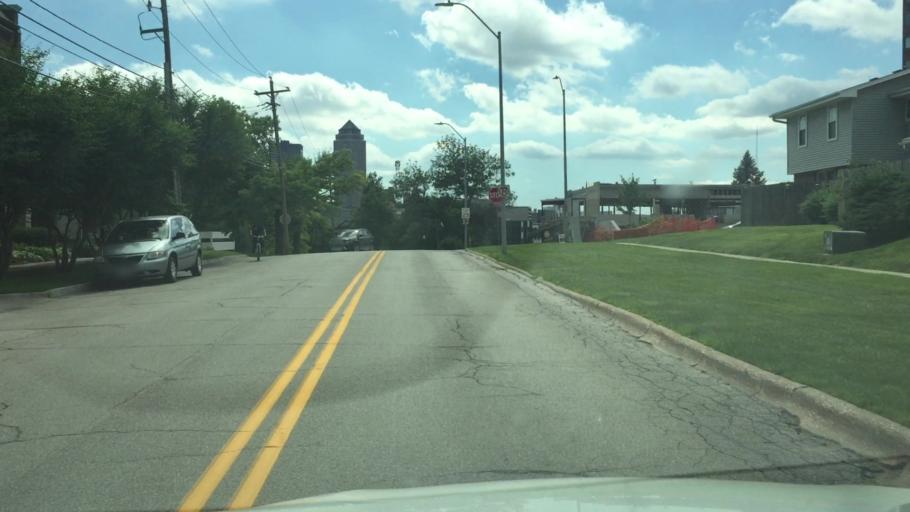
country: US
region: Iowa
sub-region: Polk County
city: Des Moines
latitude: 41.5918
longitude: -93.6114
